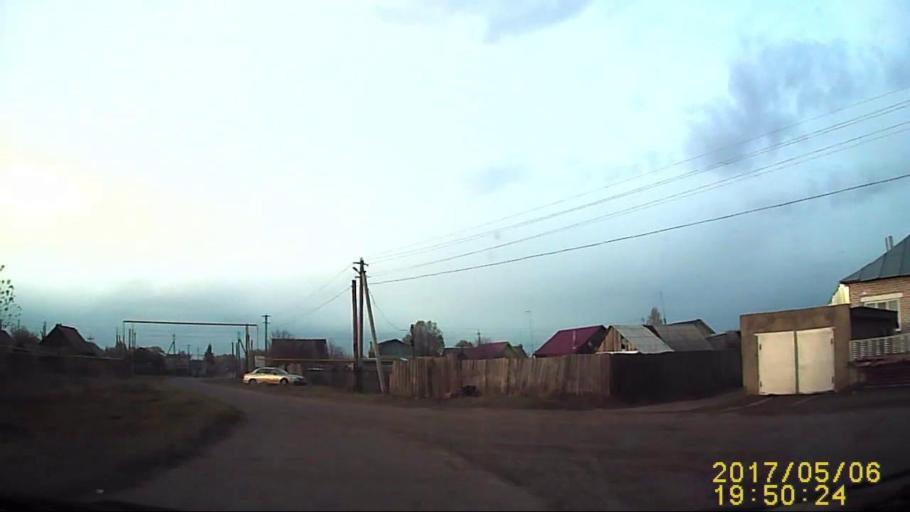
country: RU
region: Ulyanovsk
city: Staraya Mayna
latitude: 54.5998
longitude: 48.9287
